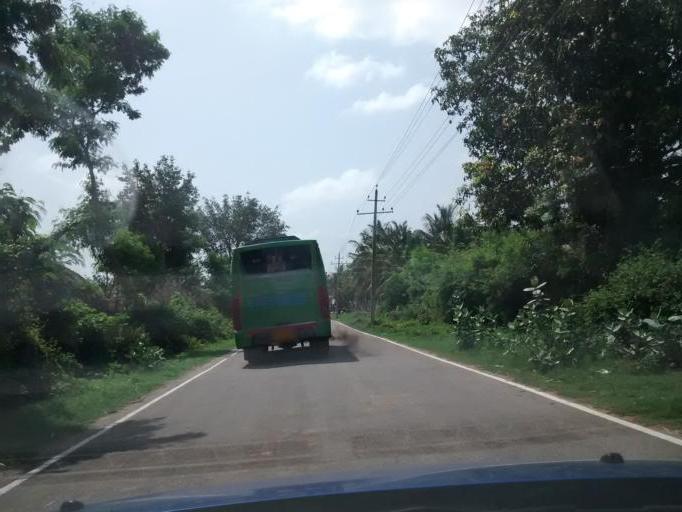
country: IN
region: Karnataka
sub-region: Hassan
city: Konanur
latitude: 12.6543
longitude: 76.1836
